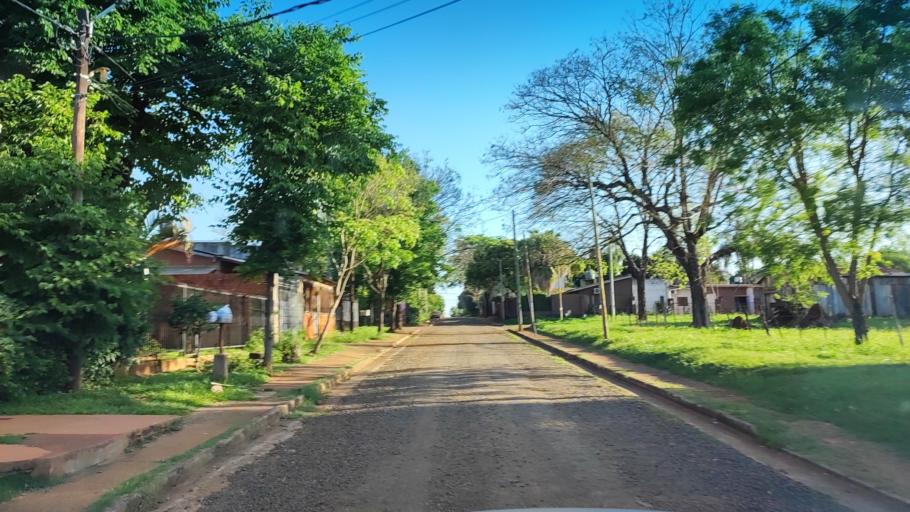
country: AR
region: Misiones
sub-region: Departamento de Capital
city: Posadas
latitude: -27.3715
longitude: -55.9418
